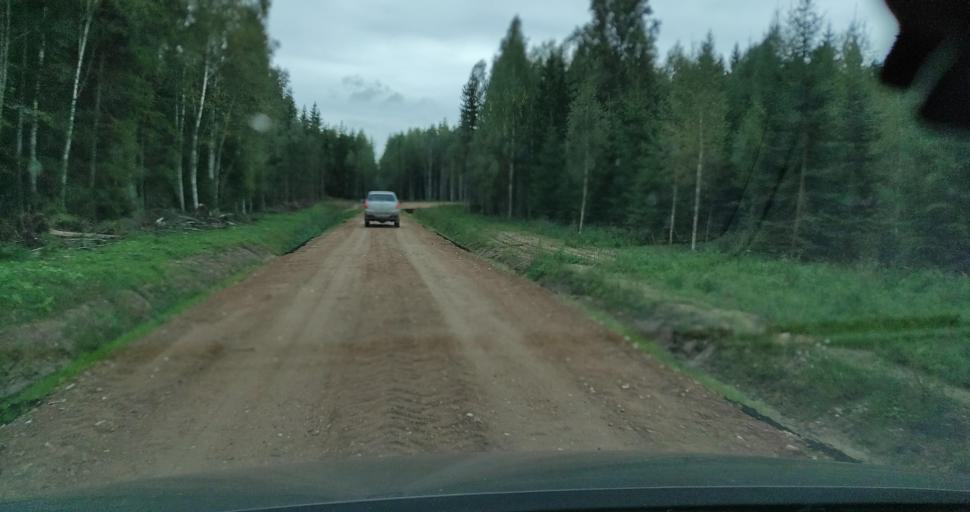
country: LV
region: Talsu Rajons
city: Sabile
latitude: 57.0154
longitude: 22.3547
